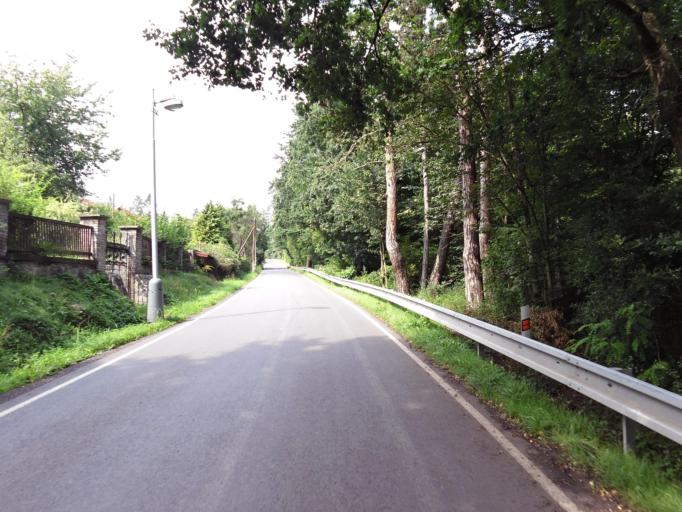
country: CZ
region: Central Bohemia
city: Kamenny Privoz
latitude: 49.8626
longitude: 14.4998
